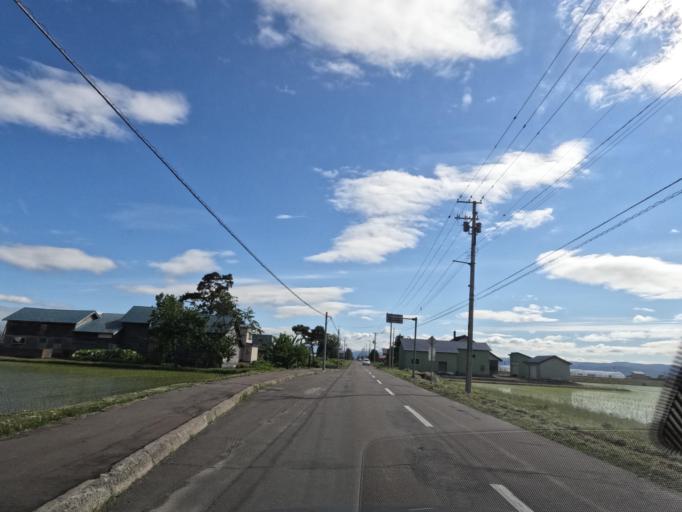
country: JP
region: Hokkaido
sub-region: Asahikawa-shi
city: Asahikawa
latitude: 43.7242
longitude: 142.5271
